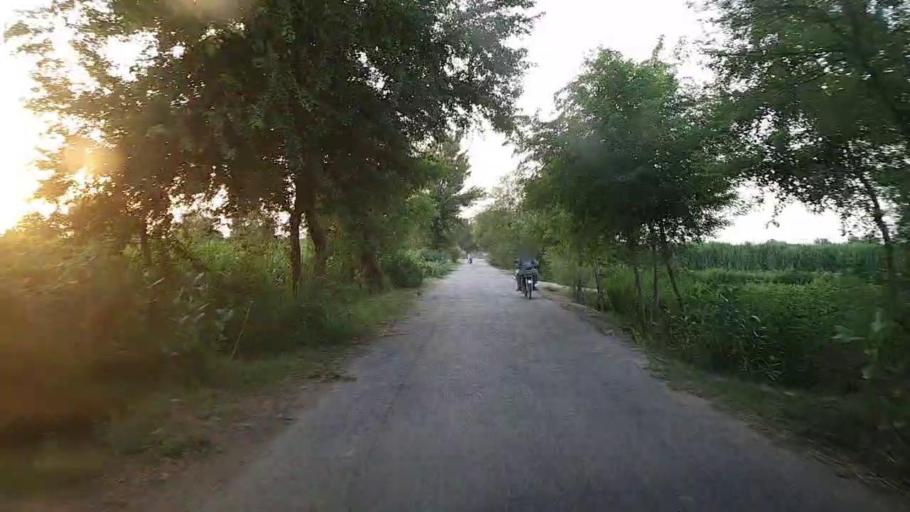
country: PK
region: Sindh
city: Ubauro
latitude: 28.3014
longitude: 69.7954
